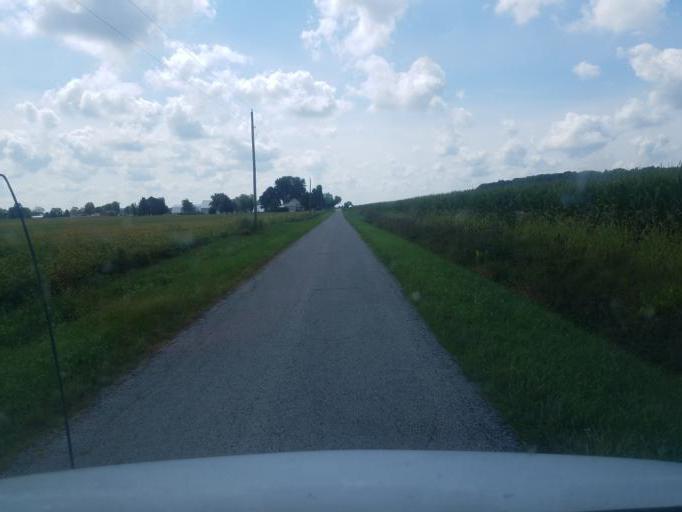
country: US
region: Ohio
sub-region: Marion County
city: Prospect
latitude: 40.4908
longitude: -83.1418
